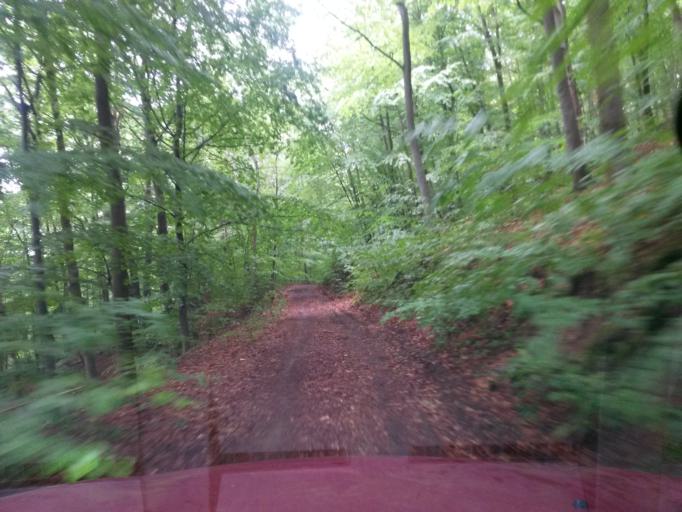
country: SK
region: Kosicky
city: Kosice
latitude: 48.7227
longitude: 21.1562
